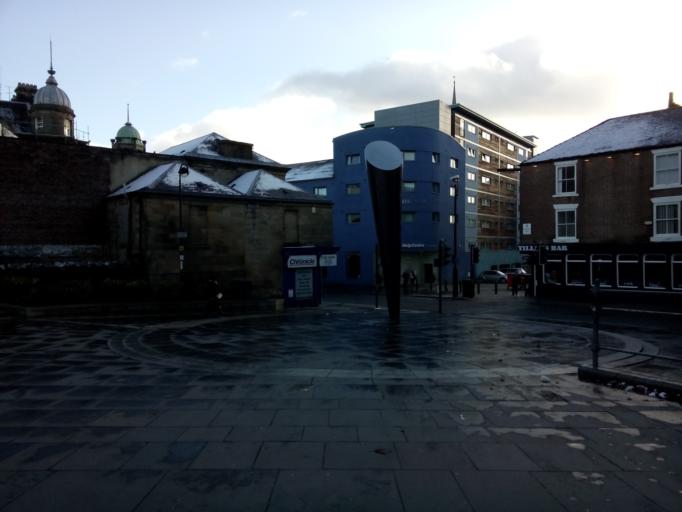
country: GB
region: England
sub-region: Newcastle upon Tyne
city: Newcastle upon Tyne
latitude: 54.9709
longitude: -1.6207
